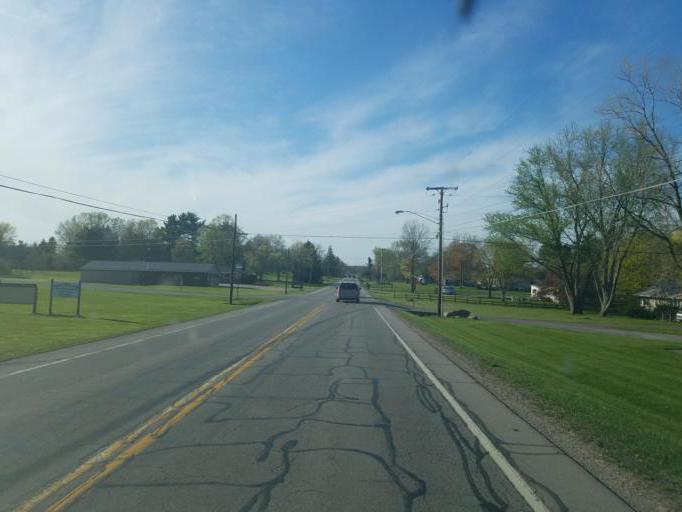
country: US
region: Ohio
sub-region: Ashland County
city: Ashland
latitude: 40.9483
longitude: -82.3607
